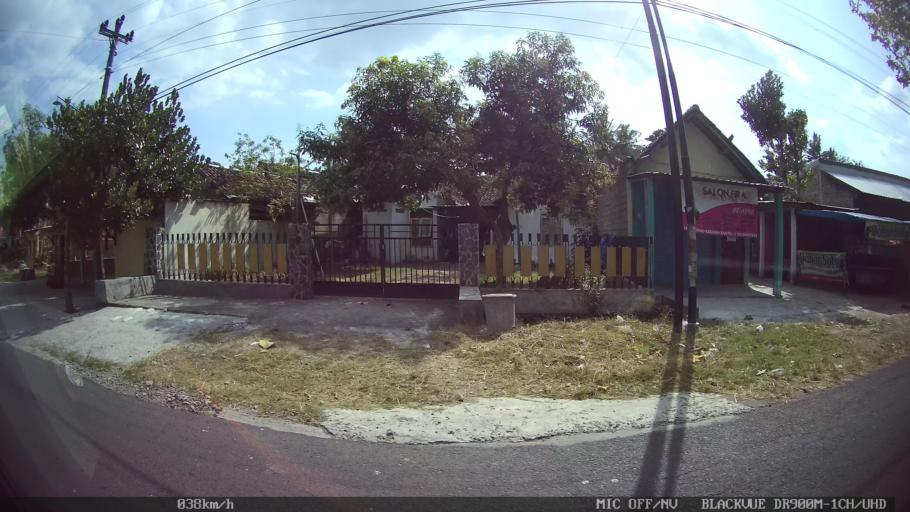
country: ID
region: Daerah Istimewa Yogyakarta
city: Kasihan
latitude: -7.8451
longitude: 110.3147
